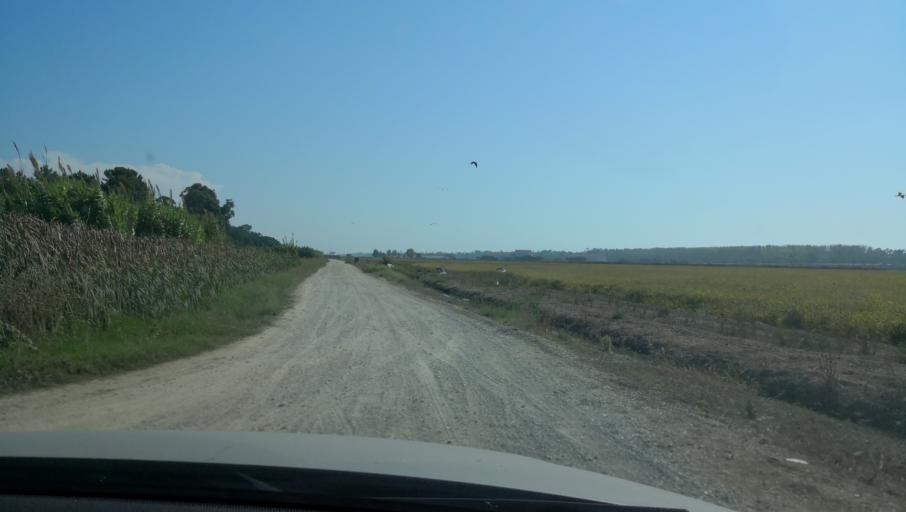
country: PT
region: Setubal
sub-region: Setubal
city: Setubal
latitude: 38.3895
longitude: -8.7898
